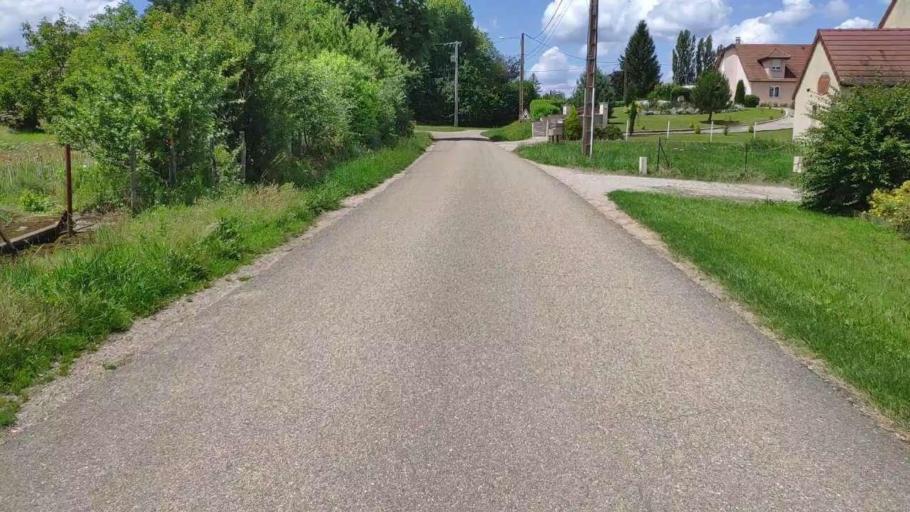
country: FR
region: Franche-Comte
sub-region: Departement du Jura
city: Bletterans
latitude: 46.8471
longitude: 5.4756
